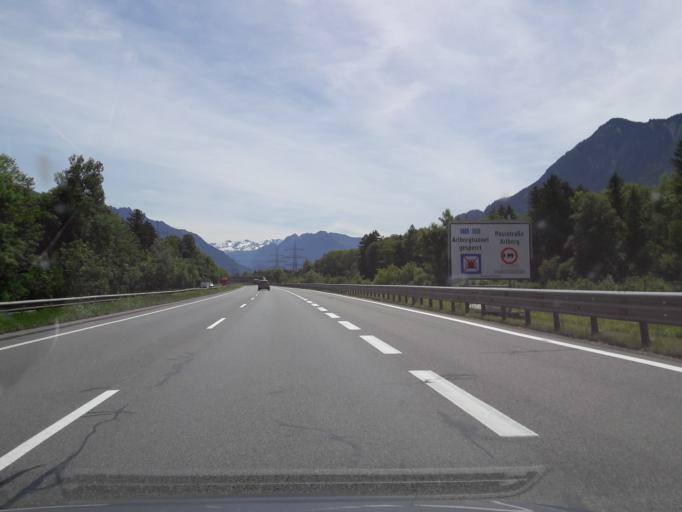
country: AT
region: Vorarlberg
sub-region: Politischer Bezirk Feldkirch
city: Schlins
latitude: 47.2003
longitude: 9.6809
